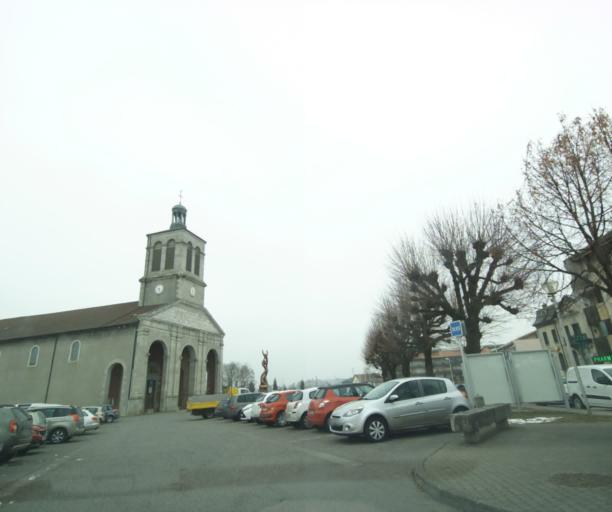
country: FR
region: Rhone-Alpes
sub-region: Departement de la Haute-Savoie
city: Reignier-Esery
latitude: 46.1377
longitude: 6.2701
